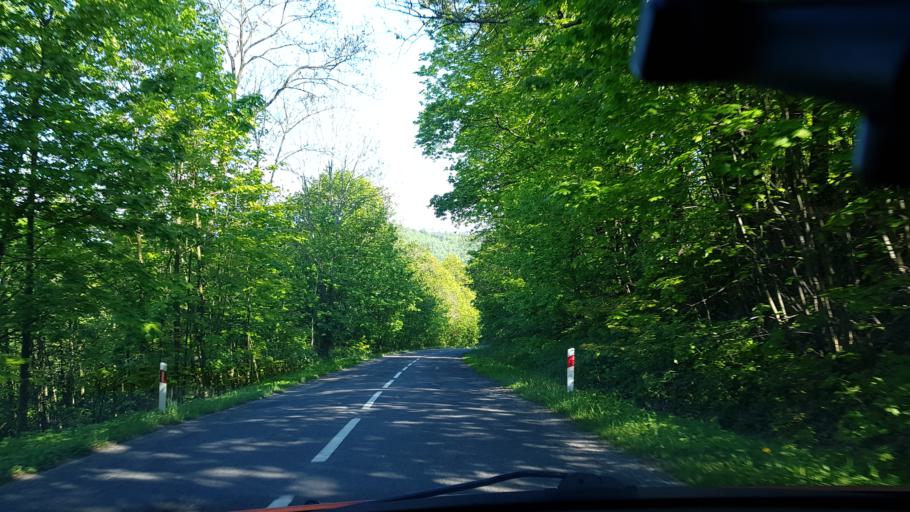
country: PL
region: Lower Silesian Voivodeship
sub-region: Powiat klodzki
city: Bozkow
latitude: 50.5713
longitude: 16.6091
